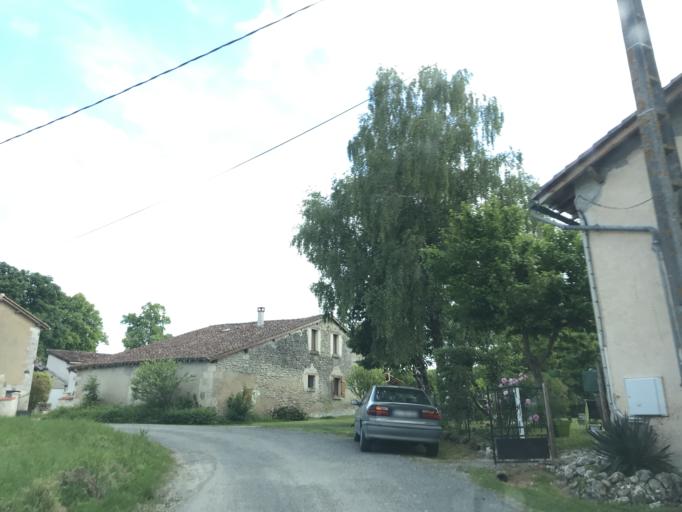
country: FR
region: Aquitaine
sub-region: Departement de la Dordogne
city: Saint-Aulaye
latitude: 45.2602
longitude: 0.1310
